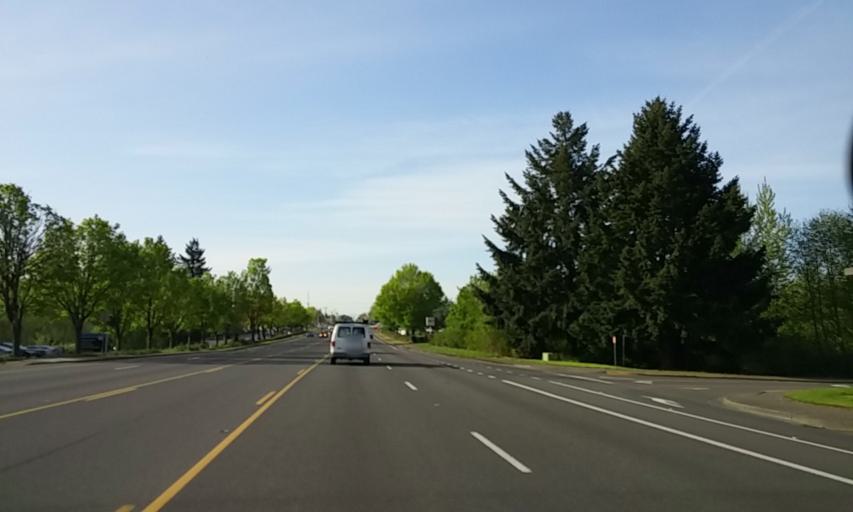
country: US
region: Oregon
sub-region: Washington County
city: Beaverton
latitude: 45.4934
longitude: -122.8264
